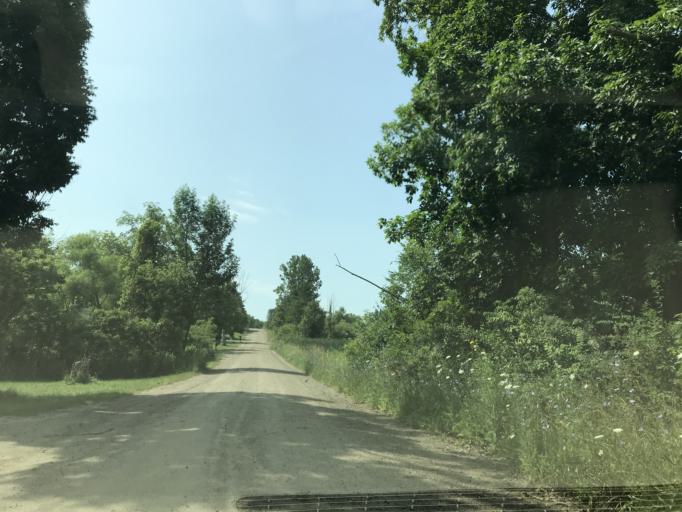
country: US
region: Michigan
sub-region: Eaton County
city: Grand Ledge
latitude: 42.7755
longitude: -84.7198
